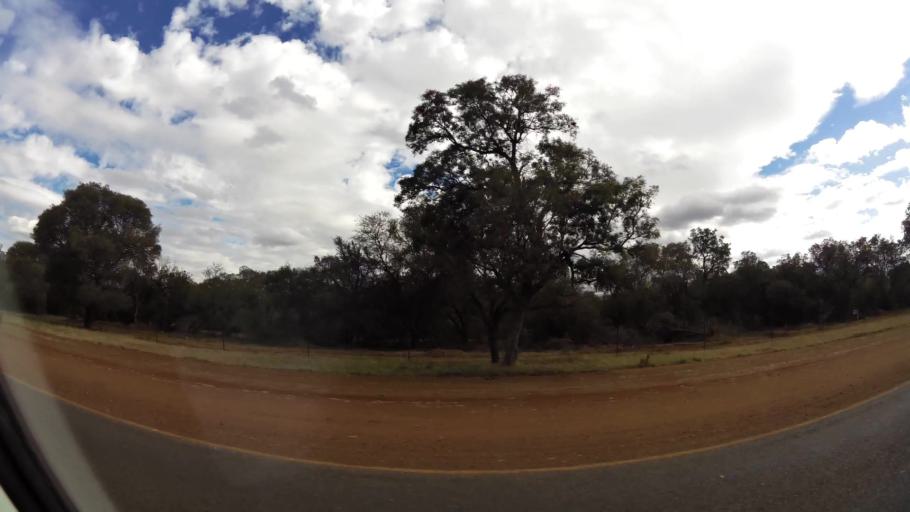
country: ZA
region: Limpopo
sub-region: Waterberg District Municipality
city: Warmbaths
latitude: -24.8974
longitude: 28.2810
